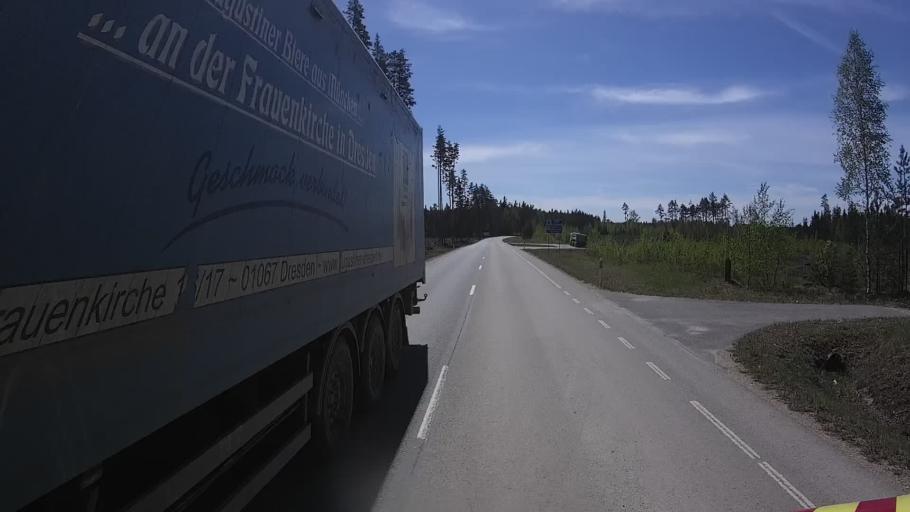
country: EE
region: Polvamaa
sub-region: Polva linn
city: Polva
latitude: 57.9230
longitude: 27.1825
